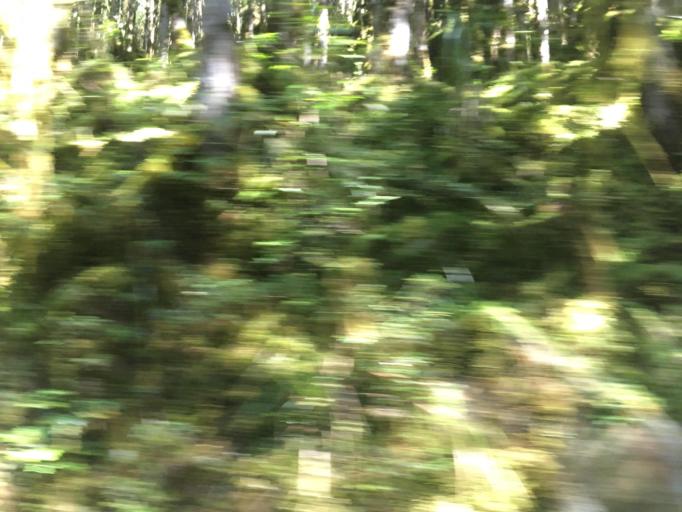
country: TW
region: Taiwan
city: Daxi
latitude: 24.5916
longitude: 121.4169
